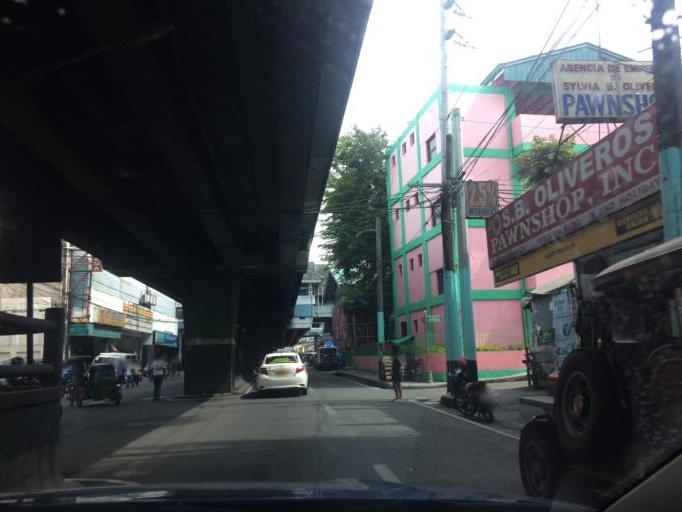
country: PH
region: Metro Manila
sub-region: Makati City
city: Makati City
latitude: 14.5490
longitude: 120.9983
